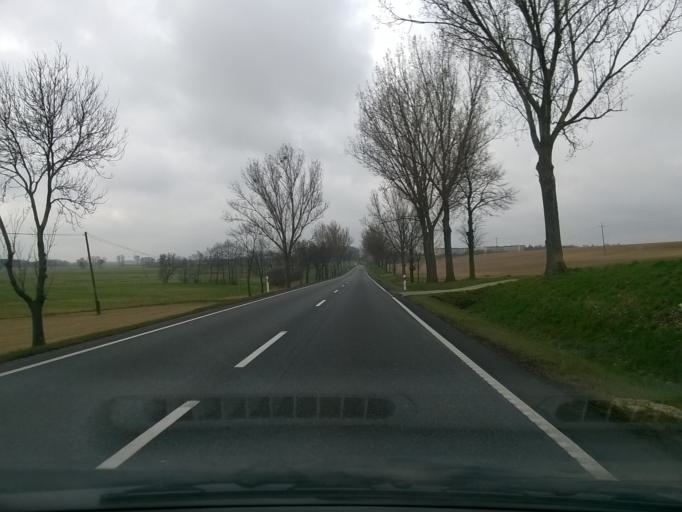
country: PL
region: Kujawsko-Pomorskie
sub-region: Powiat zninski
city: Znin
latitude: 52.8995
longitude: 17.6986
